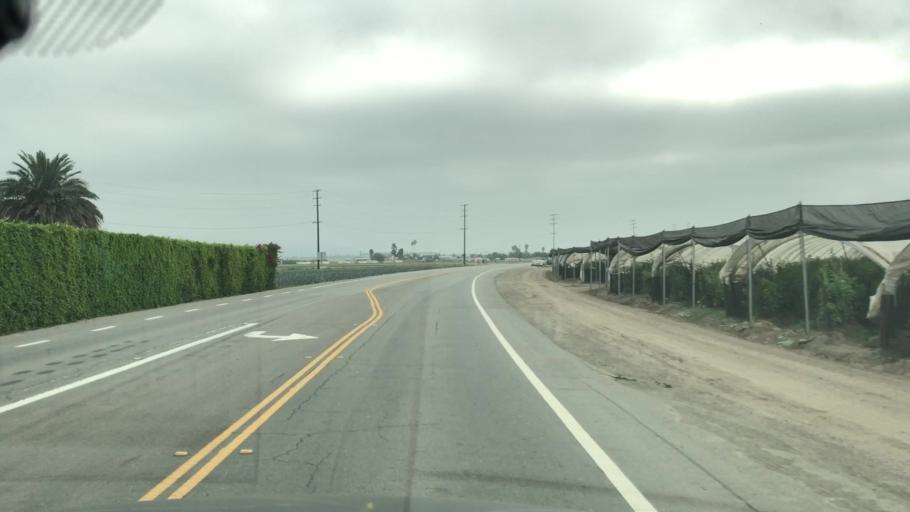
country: US
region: California
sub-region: Ventura County
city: Camarillo
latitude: 34.2045
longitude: -119.0954
